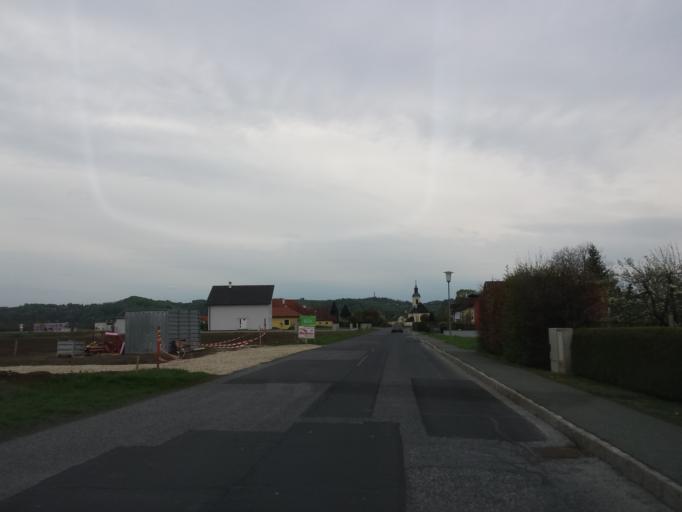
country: AT
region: Burgenland
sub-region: Politischer Bezirk Jennersdorf
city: Konigsdorf
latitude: 47.0086
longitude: 16.1742
